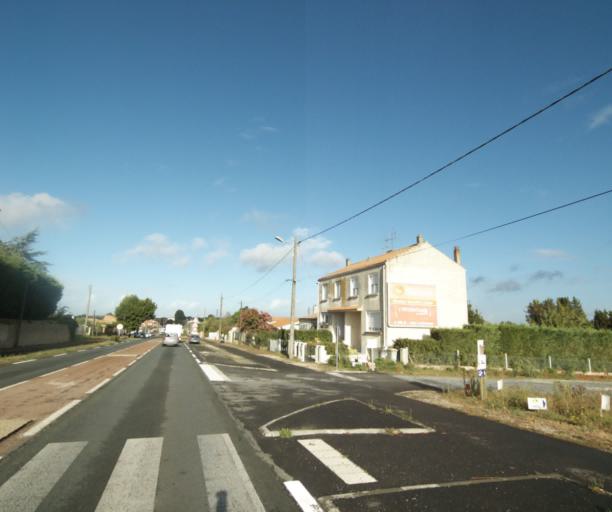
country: FR
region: Poitou-Charentes
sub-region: Departement de la Charente-Maritime
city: Tonnay-Charente
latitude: 45.9491
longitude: -0.9186
